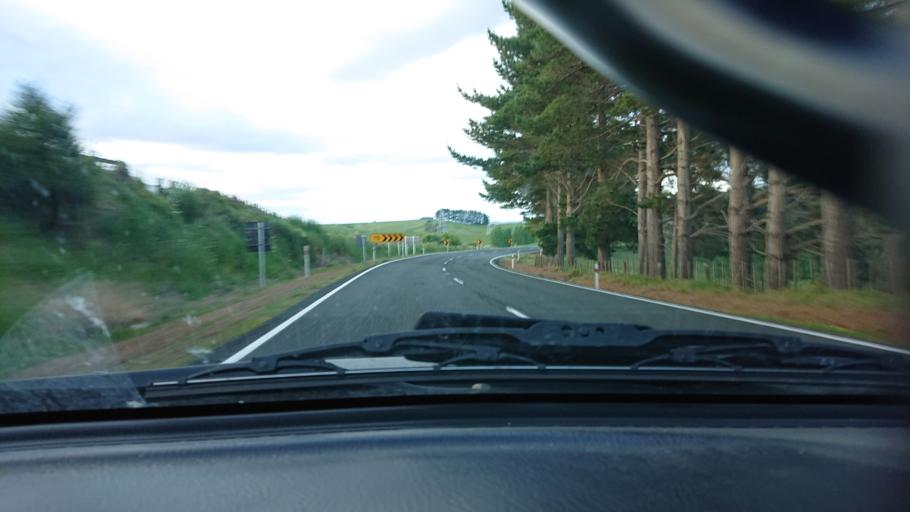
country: NZ
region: Auckland
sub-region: Auckland
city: Parakai
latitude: -36.4688
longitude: 174.4471
